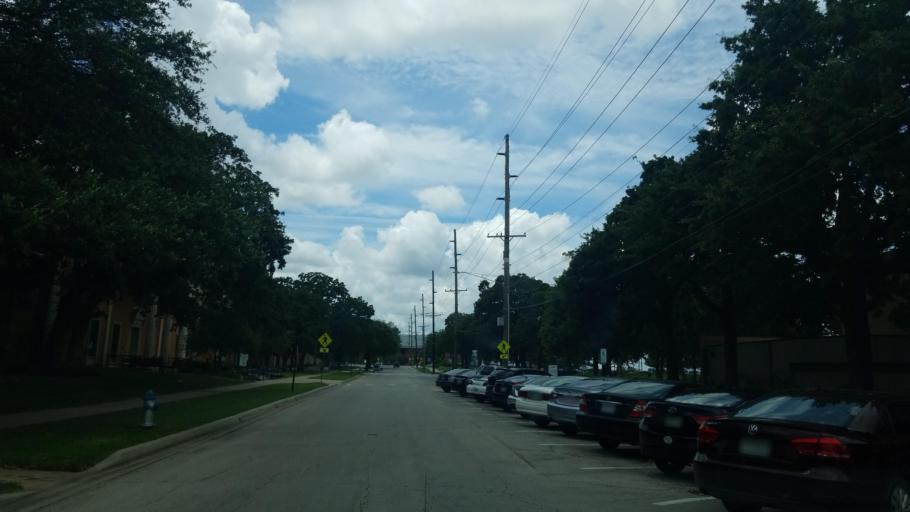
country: US
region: Texas
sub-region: Denton County
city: Denton
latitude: 33.2083
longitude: -97.1493
